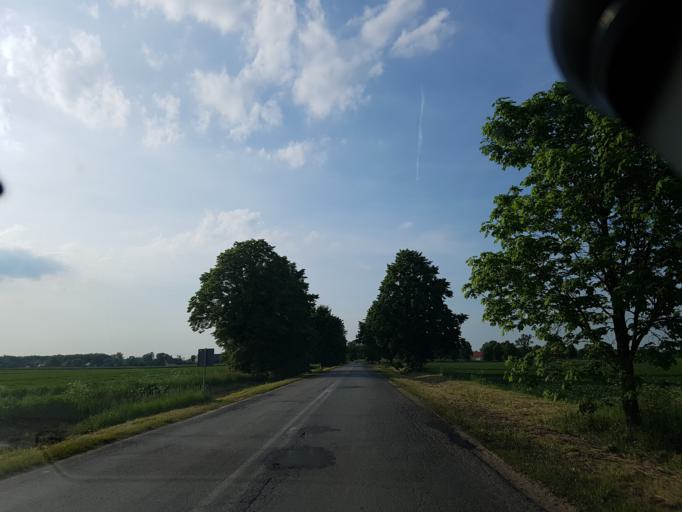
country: PL
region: Lower Silesian Voivodeship
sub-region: Powiat wroclawski
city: Kobierzyce
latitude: 50.9249
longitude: 16.9478
